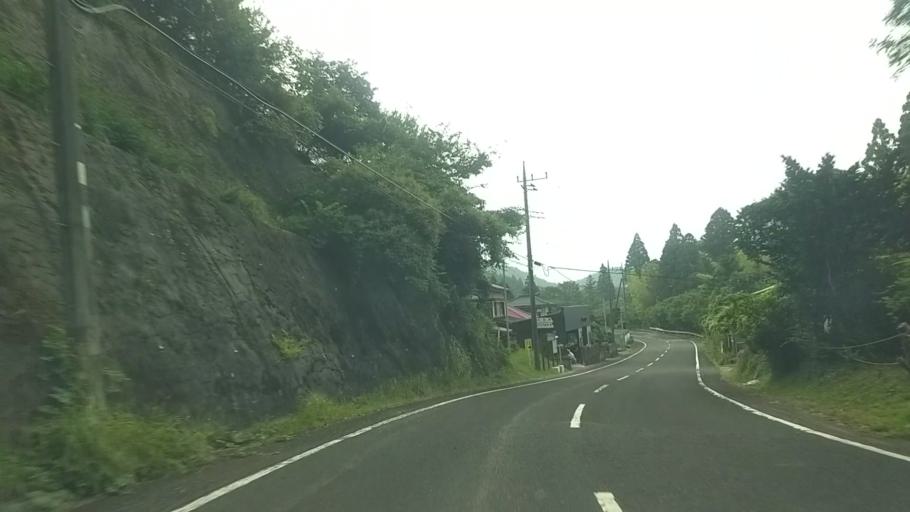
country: JP
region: Chiba
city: Kawaguchi
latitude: 35.1725
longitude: 140.1339
